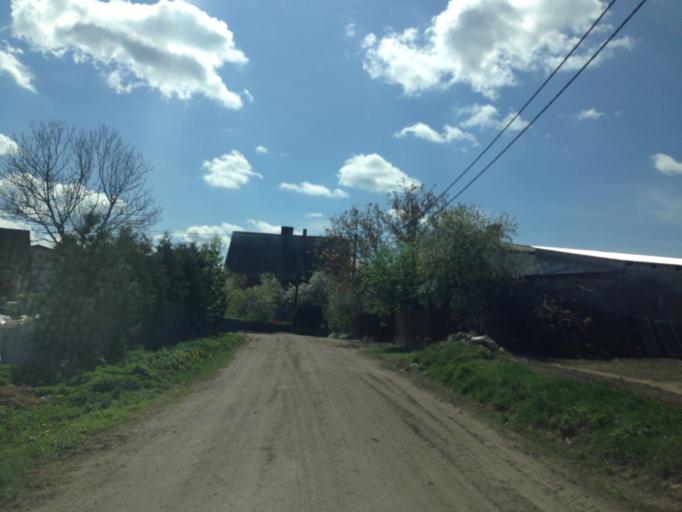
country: PL
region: Kujawsko-Pomorskie
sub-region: Powiat brodnicki
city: Brzozie
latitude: 53.2962
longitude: 19.6599
